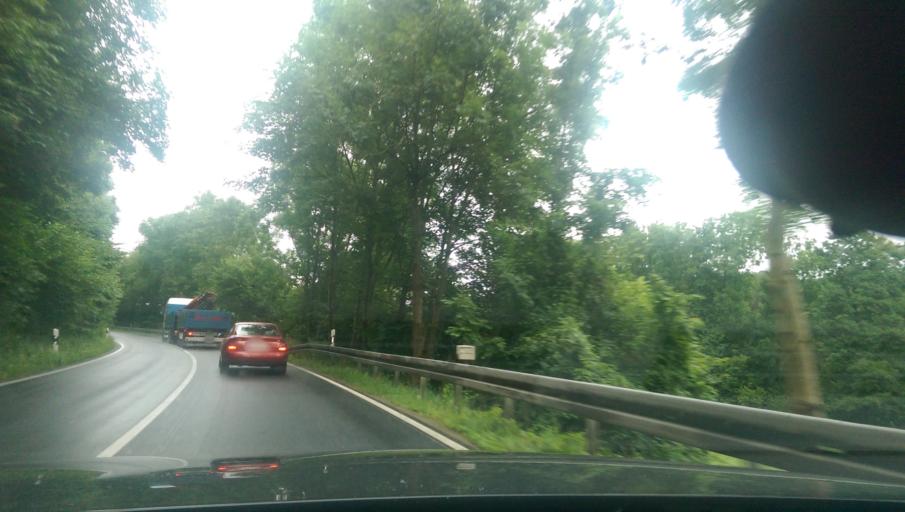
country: DE
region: Hesse
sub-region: Regierungsbezirk Kassel
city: Grossalmerode
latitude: 51.2738
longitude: 9.8440
